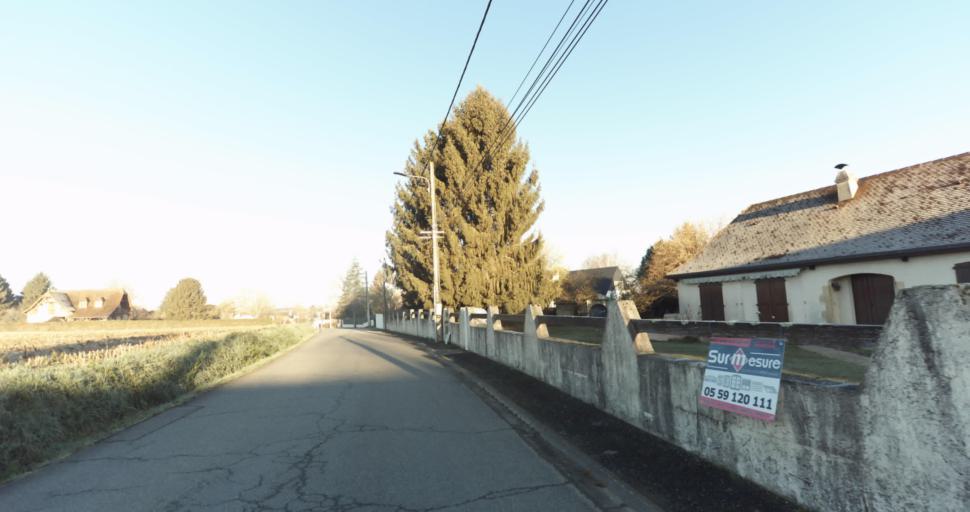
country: FR
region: Aquitaine
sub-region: Departement des Pyrenees-Atlantiques
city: Morlaas
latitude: 43.3339
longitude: -0.2709
